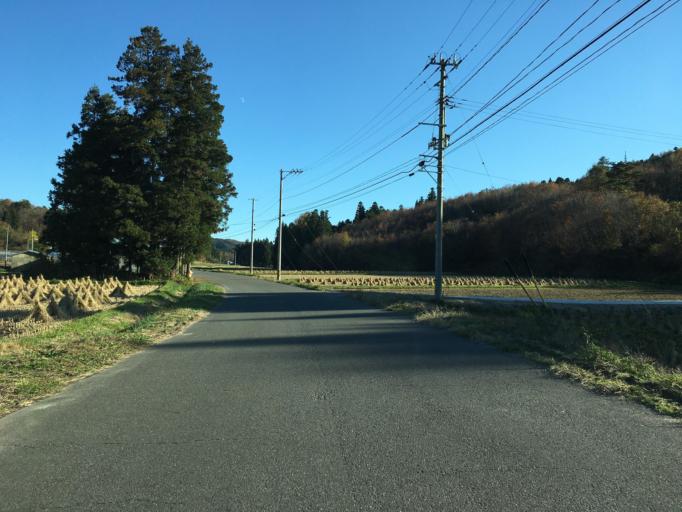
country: JP
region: Fukushima
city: Ishikawa
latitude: 37.2405
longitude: 140.5393
